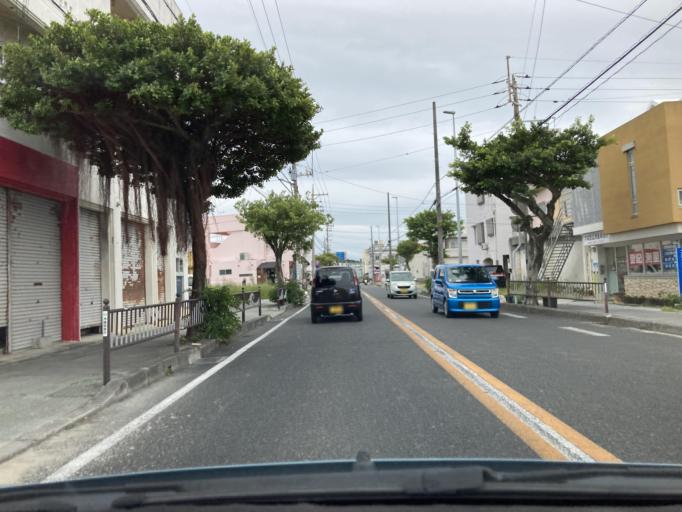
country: JP
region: Okinawa
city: Itoman
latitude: 26.1279
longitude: 127.6689
